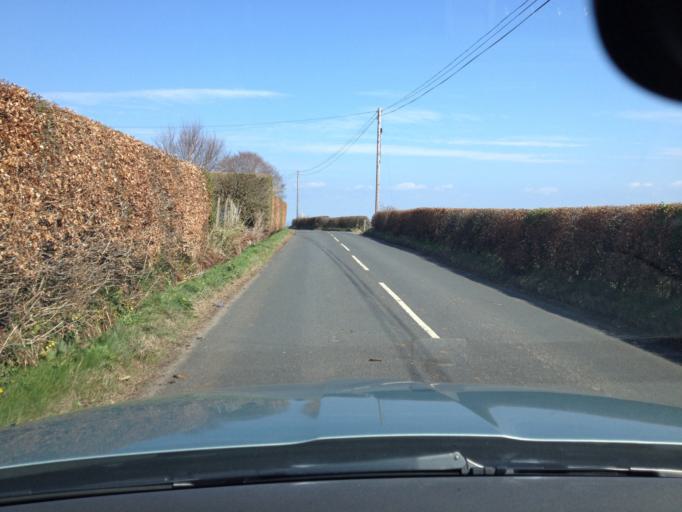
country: GB
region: Scotland
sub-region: North Ayrshire
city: Lamlash
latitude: 55.4559
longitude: -5.0920
